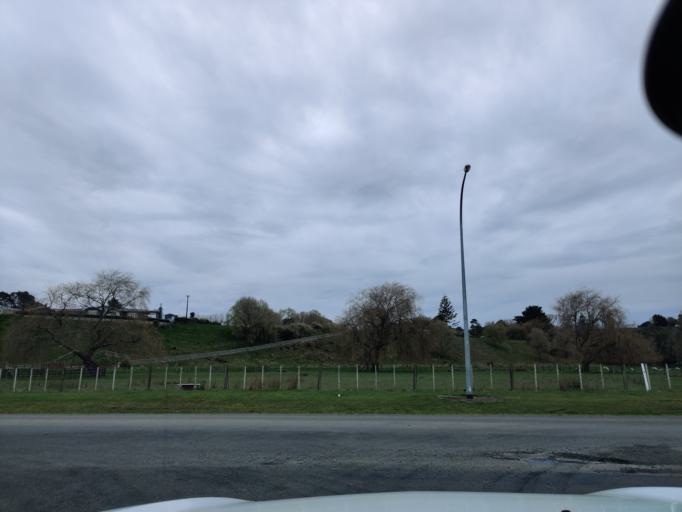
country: NZ
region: Manawatu-Wanganui
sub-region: Palmerston North City
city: Palmerston North
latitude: -40.2850
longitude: 175.7490
